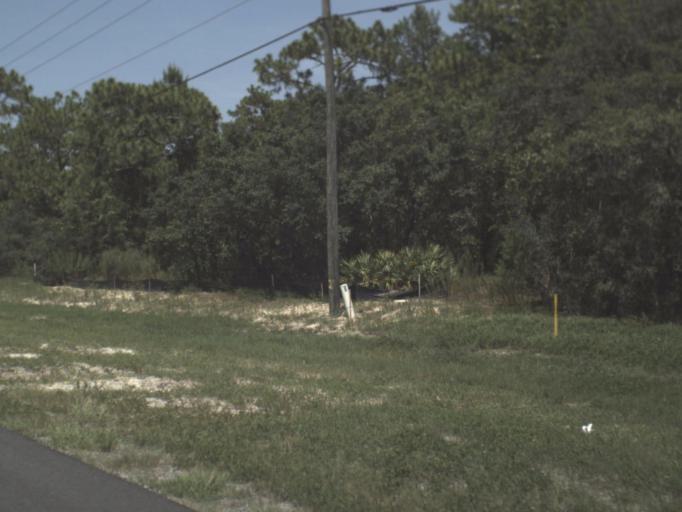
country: US
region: Florida
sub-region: Hernando County
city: Hernando Beach
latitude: 28.4254
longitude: -82.6438
